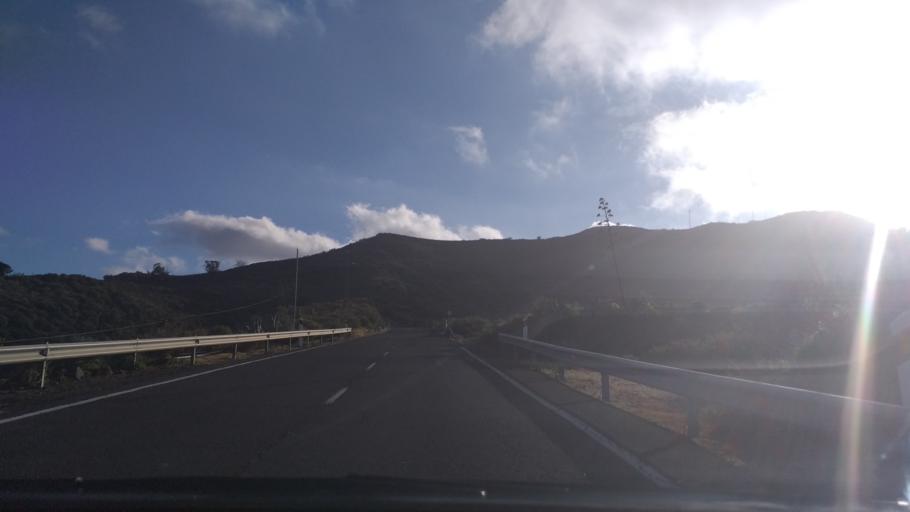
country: ES
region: Canary Islands
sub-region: Provincia de Las Palmas
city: Valsequillo de Gran Canaria
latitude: 27.9617
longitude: -15.4910
